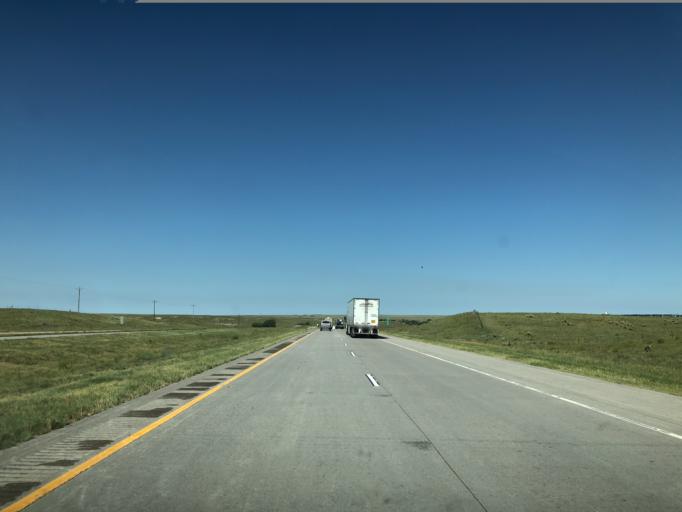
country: US
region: Colorado
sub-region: Lincoln County
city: Hugo
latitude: 39.2751
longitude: -102.9801
